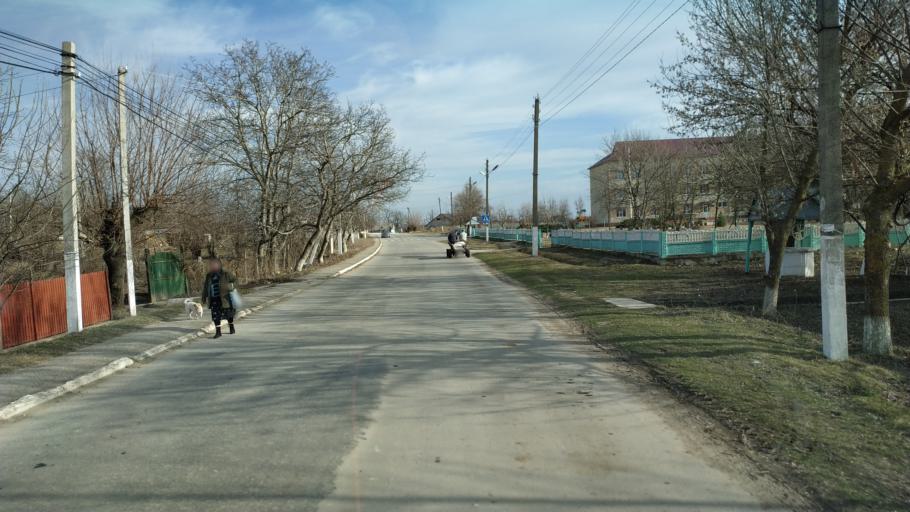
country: RO
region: Iasi
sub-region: Comuna Gorban
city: Gorban
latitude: 46.9077
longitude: 28.1181
